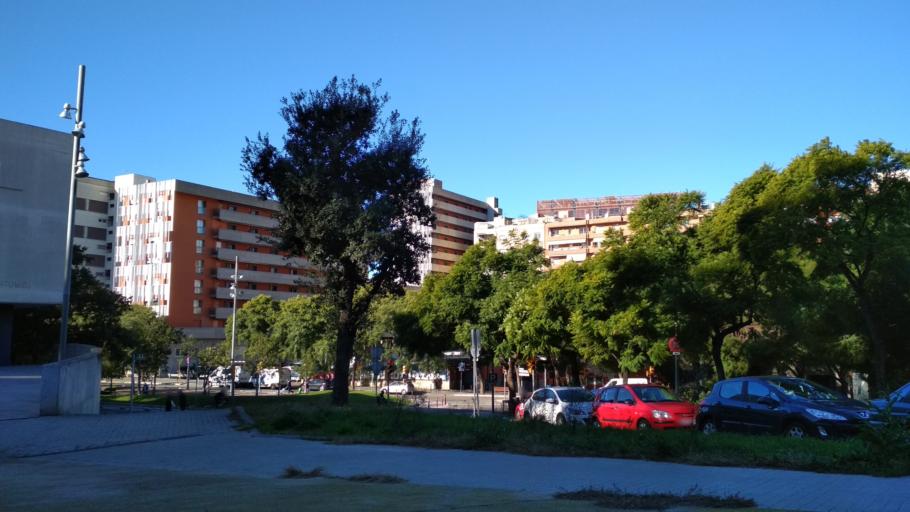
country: ES
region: Catalonia
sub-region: Provincia de Barcelona
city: Sants-Montjuic
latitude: 41.3658
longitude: 2.1404
